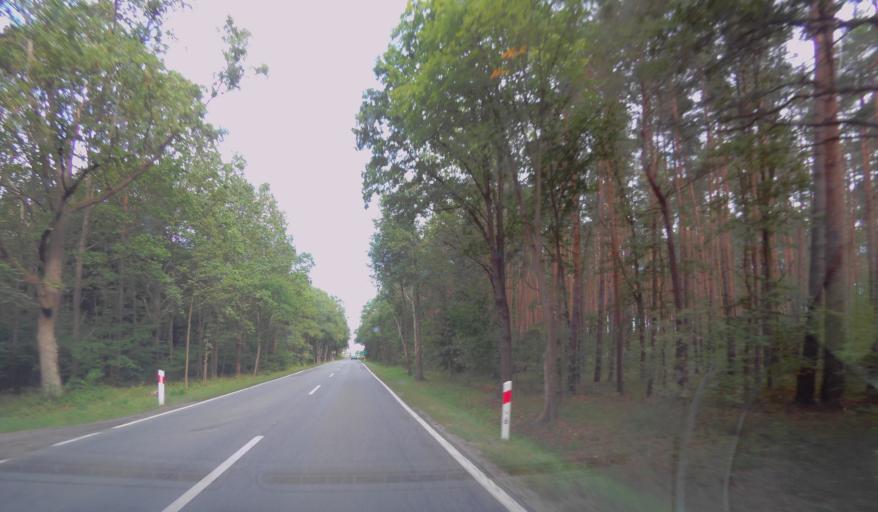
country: PL
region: Subcarpathian Voivodeship
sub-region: Powiat nizanski
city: Krzeszow
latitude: 50.3951
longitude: 22.2993
